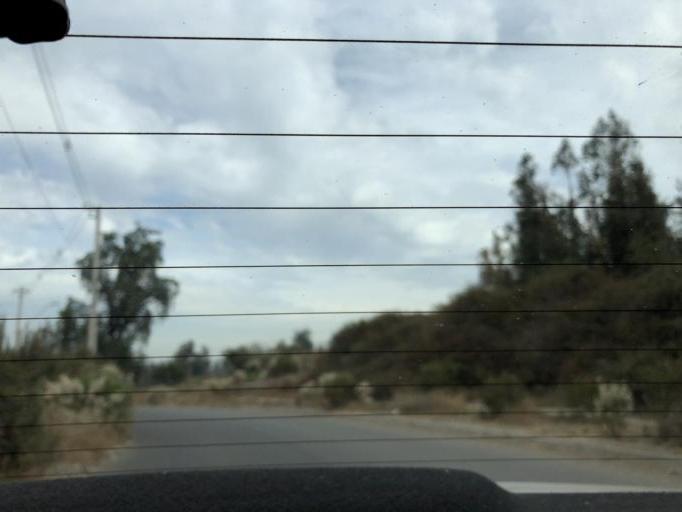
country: CL
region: Santiago Metropolitan
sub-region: Provincia de Cordillera
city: Puente Alto
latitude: -33.5931
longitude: -70.5205
